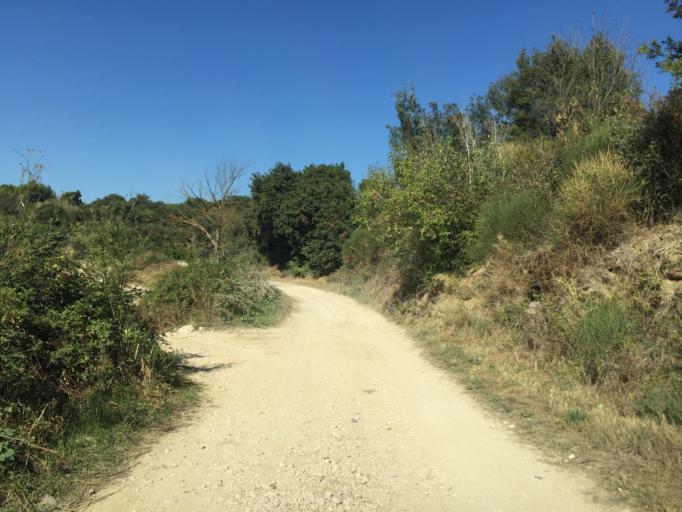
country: FR
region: Provence-Alpes-Cote d'Azur
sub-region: Departement du Vaucluse
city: Chateauneuf-du-Pape
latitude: 44.0661
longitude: 4.8220
